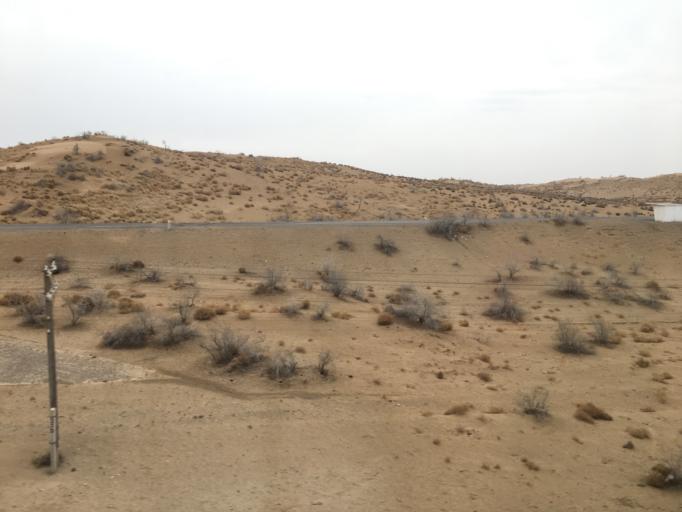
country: TM
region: Mary
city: Yoloeten
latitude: 36.4471
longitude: 62.5882
